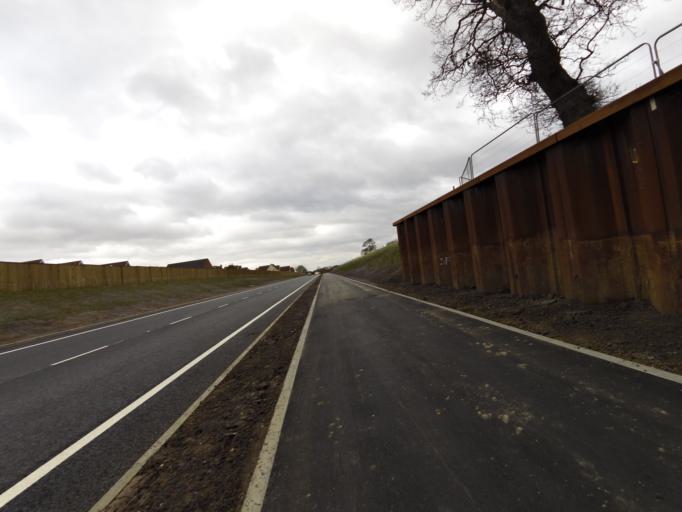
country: GB
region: England
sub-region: Norfolk
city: Hopton on Sea
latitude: 52.5023
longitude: 1.7278
